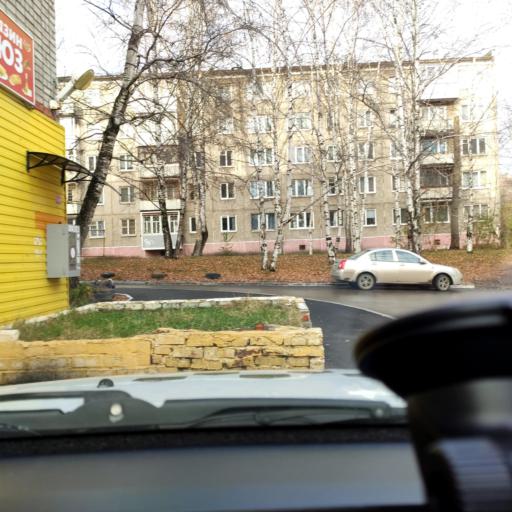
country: RU
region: Perm
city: Perm
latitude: 57.9800
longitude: 56.2220
